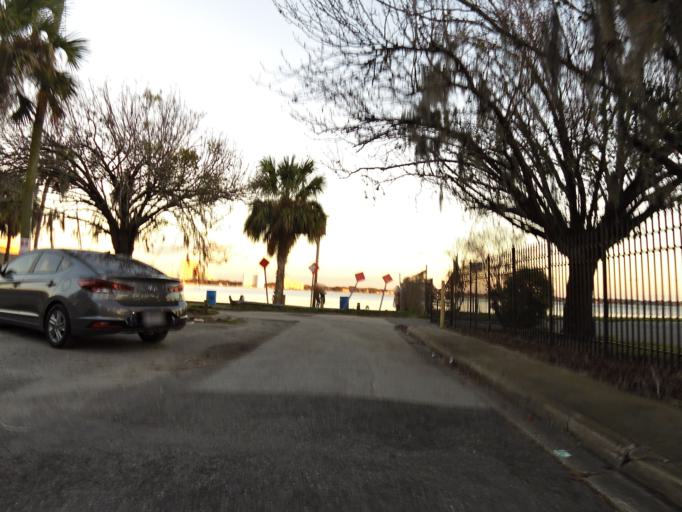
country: US
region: Florida
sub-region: Duval County
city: Jacksonville
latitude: 30.3139
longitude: -81.6766
